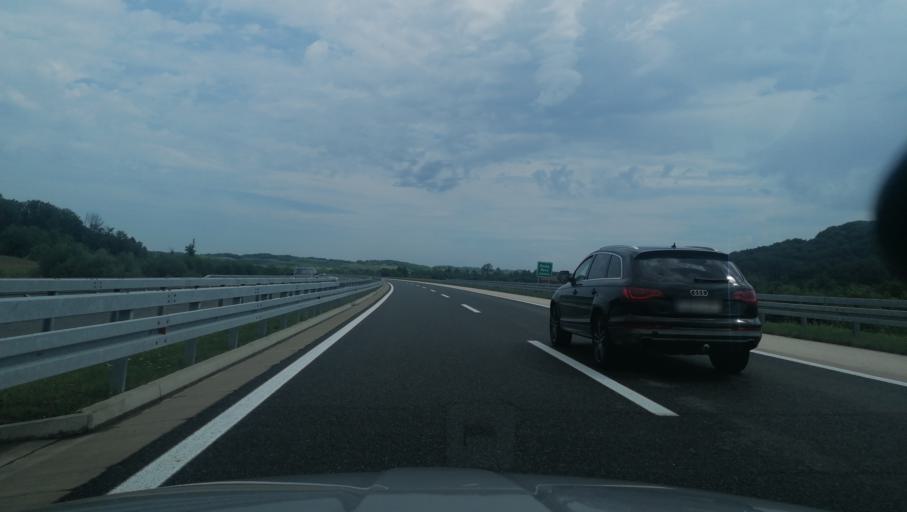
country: BA
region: Republika Srpska
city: Stanari
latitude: 44.8203
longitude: 17.9238
